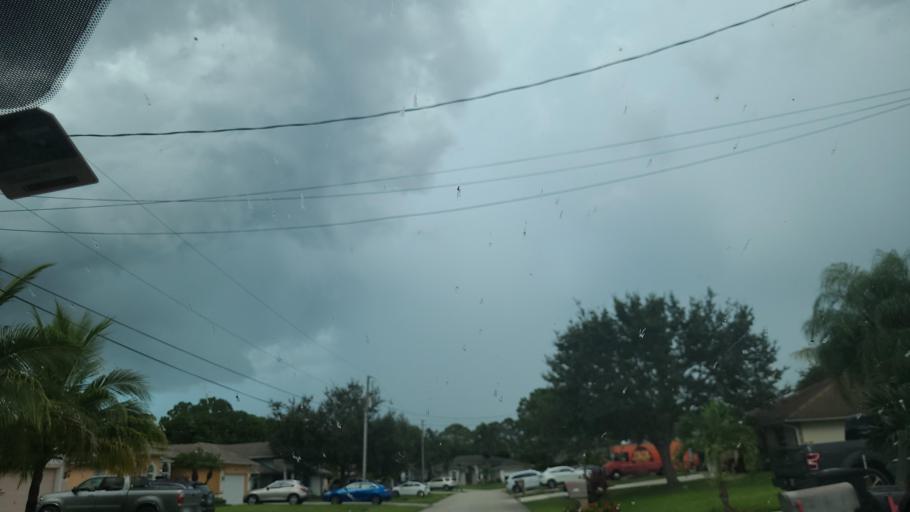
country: US
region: Florida
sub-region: Saint Lucie County
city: Port Saint Lucie
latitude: 27.2530
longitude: -80.4037
